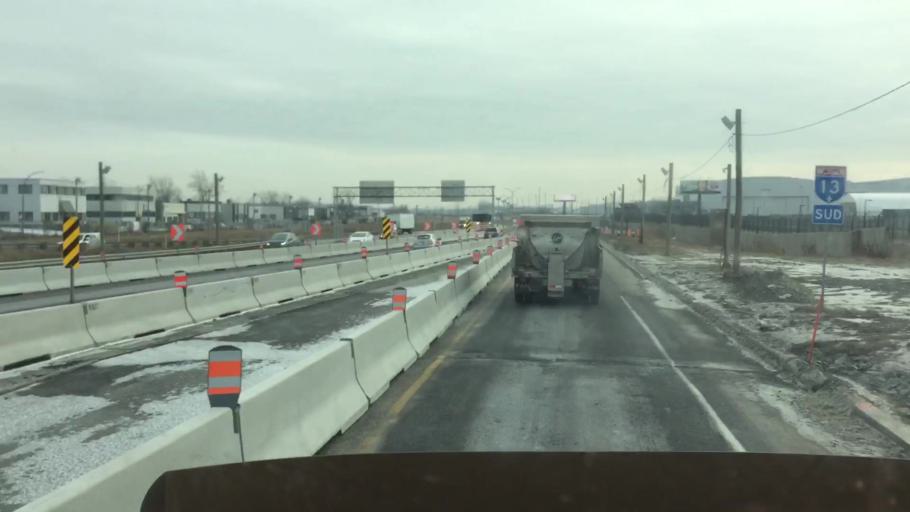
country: CA
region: Quebec
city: Dorval
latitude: 45.4869
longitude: -73.7316
